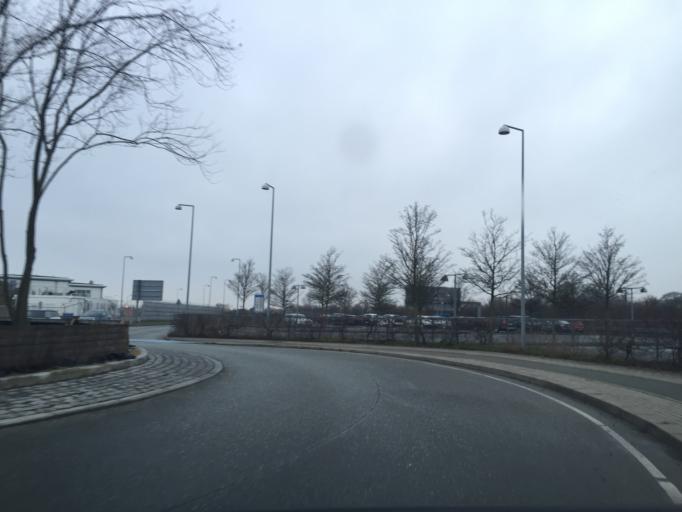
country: DK
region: Capital Region
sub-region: Tarnby Kommune
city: Tarnby
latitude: 55.6294
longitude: 12.6283
